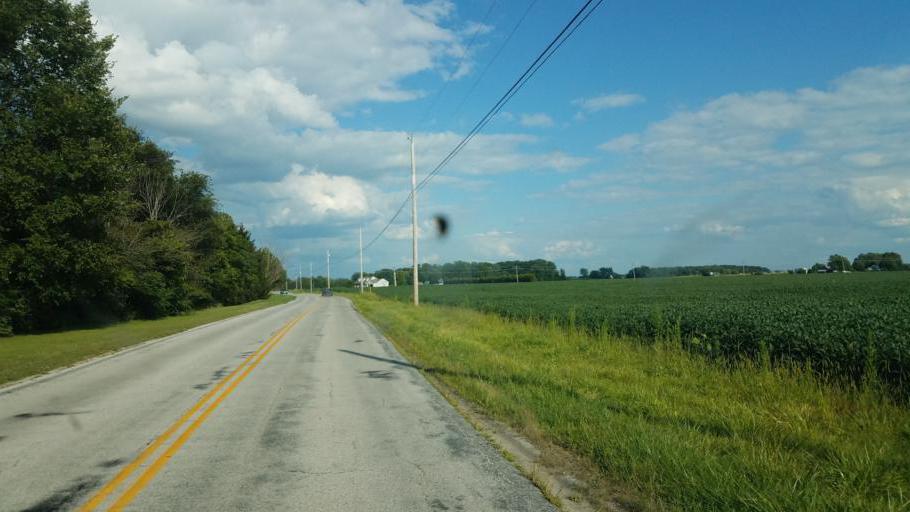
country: US
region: Ohio
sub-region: Wood County
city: Bowling Green
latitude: 41.3611
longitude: -83.5956
